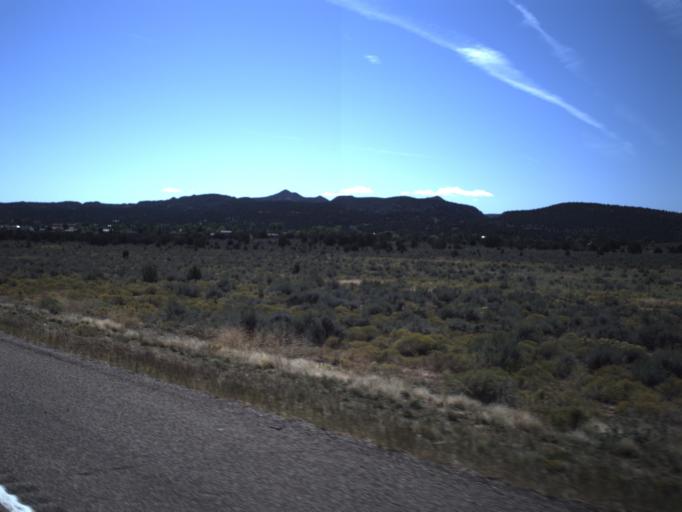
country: US
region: Utah
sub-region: Washington County
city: Ivins
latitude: 37.3154
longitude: -113.6777
